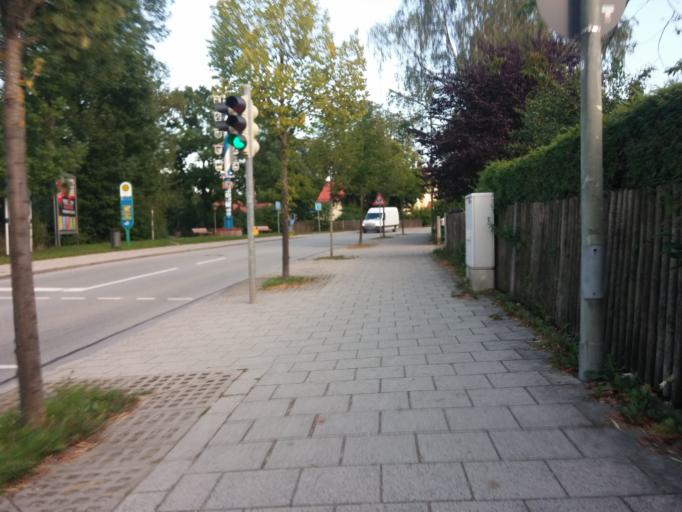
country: DE
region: Bavaria
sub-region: Upper Bavaria
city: Feldkirchen
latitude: 48.1279
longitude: 11.7406
